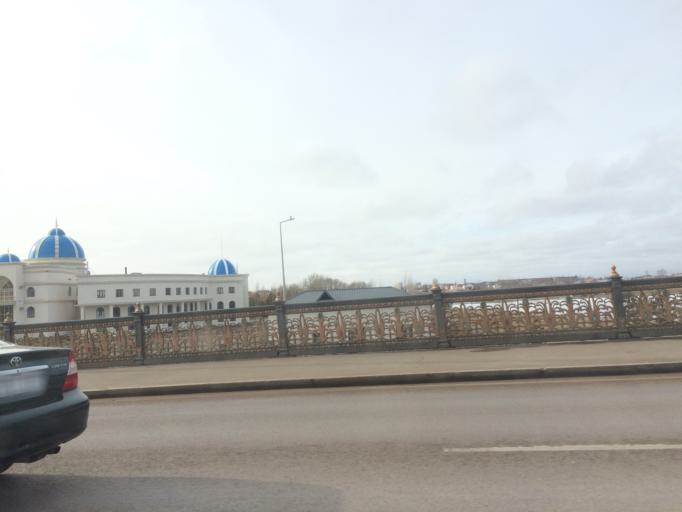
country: KZ
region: Astana Qalasy
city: Astana
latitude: 51.1565
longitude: 71.4117
